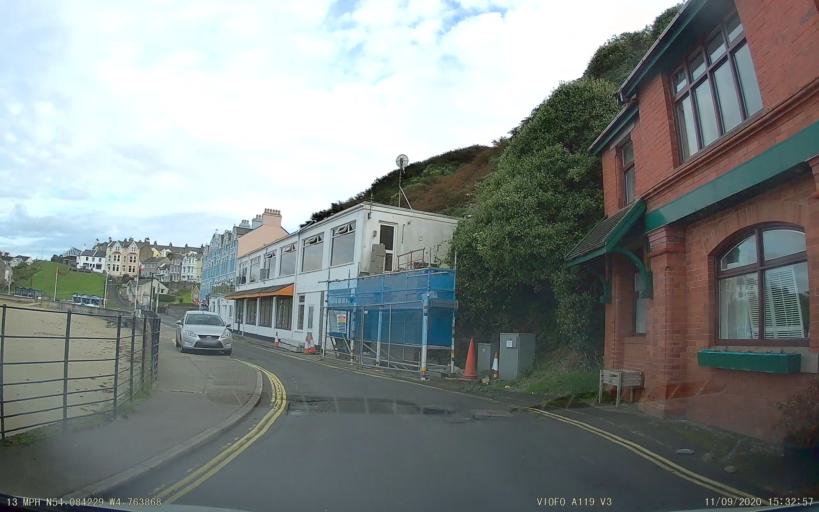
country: IM
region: Port Erin
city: Port Erin
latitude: 54.0837
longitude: -4.7635
